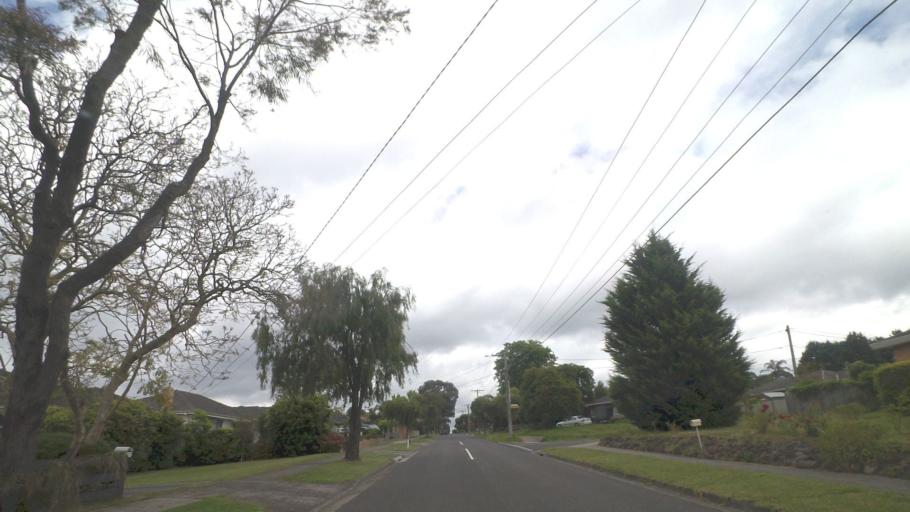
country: AU
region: Victoria
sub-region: Maroondah
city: Heathmont
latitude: -37.8441
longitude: 145.2554
